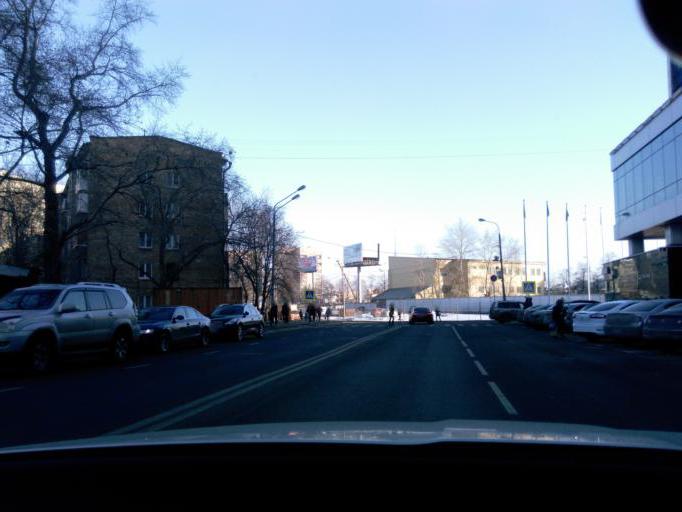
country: RU
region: Moscow
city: Mar'ina Roshcha
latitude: 55.7905
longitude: 37.5843
